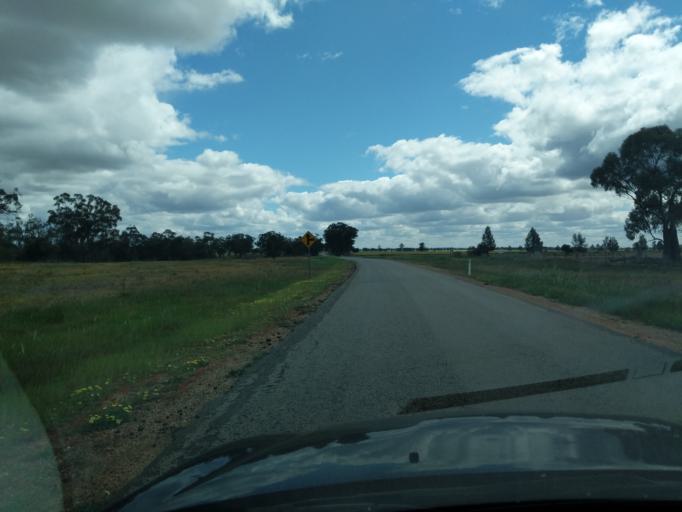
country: AU
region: New South Wales
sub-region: Coolamon
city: Coolamon
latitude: -34.8687
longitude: 146.8982
